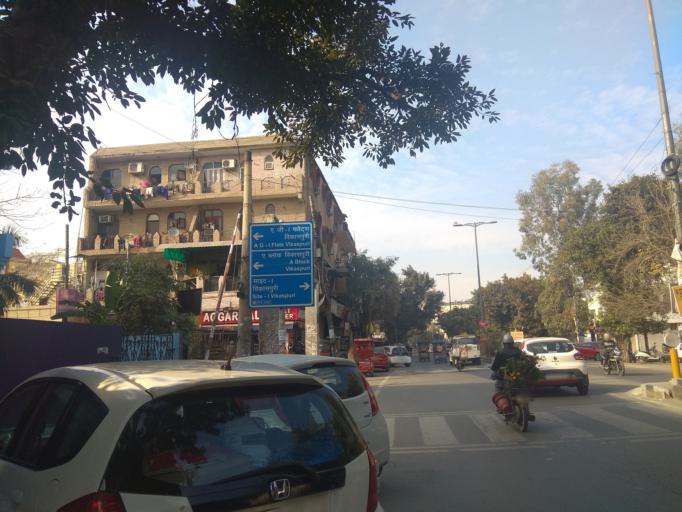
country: IN
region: NCT
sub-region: West Delhi
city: Nangloi Jat
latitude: 28.6283
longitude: 77.0694
